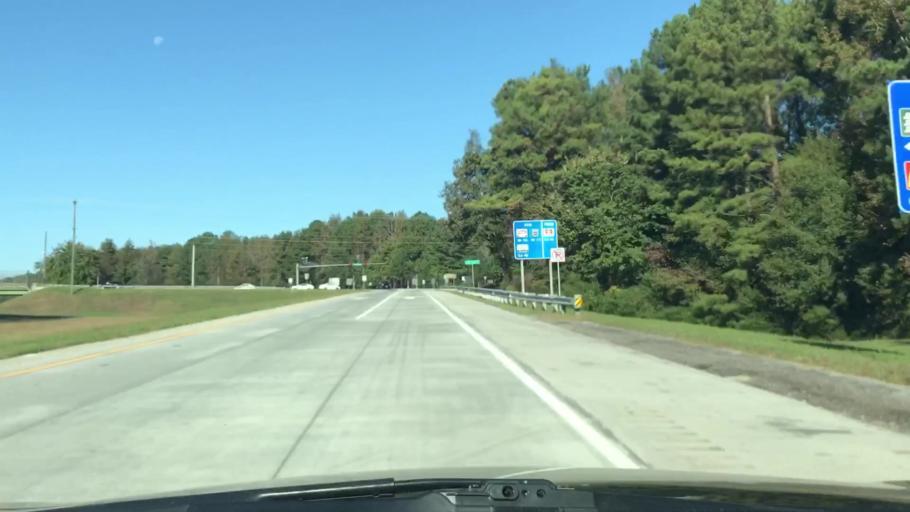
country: US
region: Georgia
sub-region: Carroll County
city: Villa Rica
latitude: 33.7252
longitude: -84.8987
